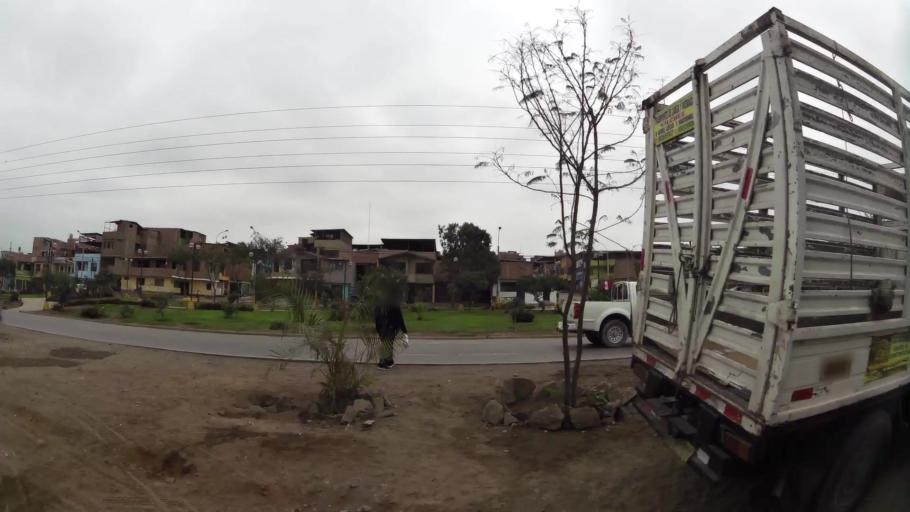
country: PE
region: Lima
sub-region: Lima
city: Surco
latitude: -12.1935
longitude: -76.9501
